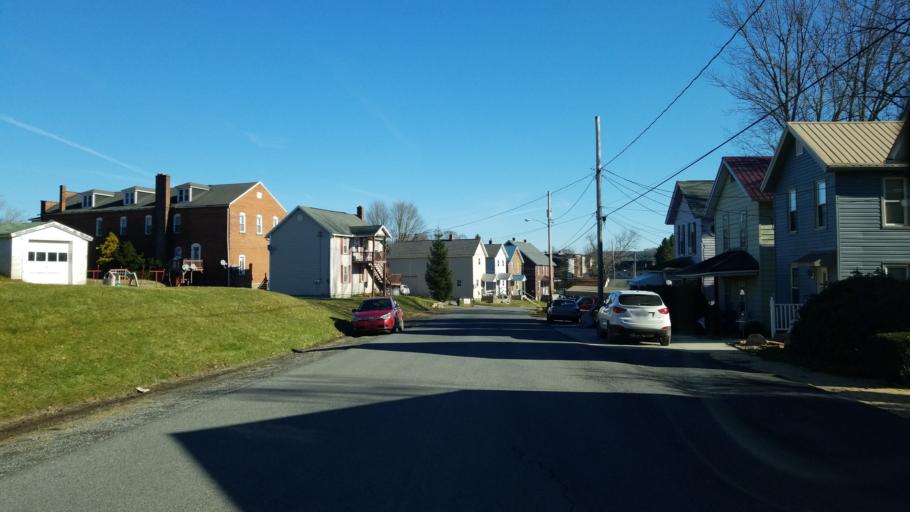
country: US
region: Pennsylvania
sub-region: Jefferson County
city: Falls Creek
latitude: 41.1442
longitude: -78.8019
